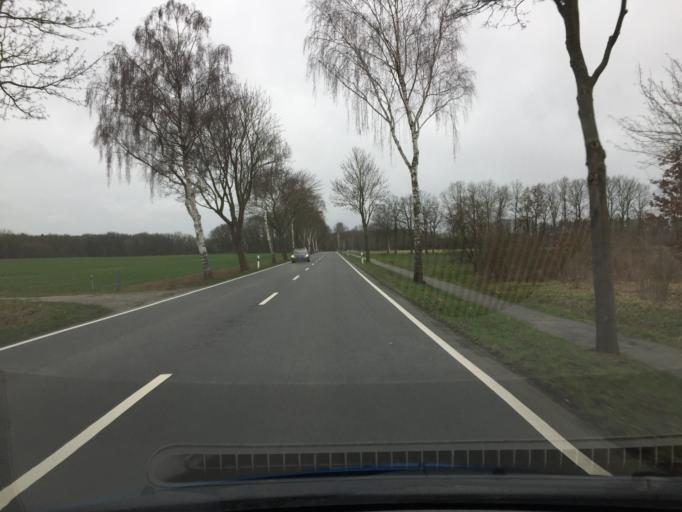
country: DE
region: Lower Saxony
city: Ratzlingen
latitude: 52.9884
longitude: 10.6358
